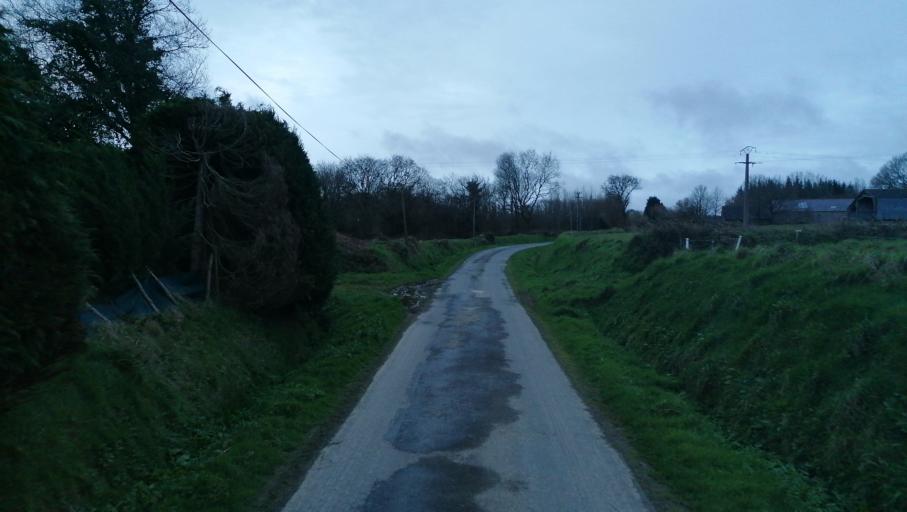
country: FR
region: Brittany
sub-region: Departement des Cotes-d'Armor
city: Goudelin
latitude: 48.5781
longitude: -3.0536
